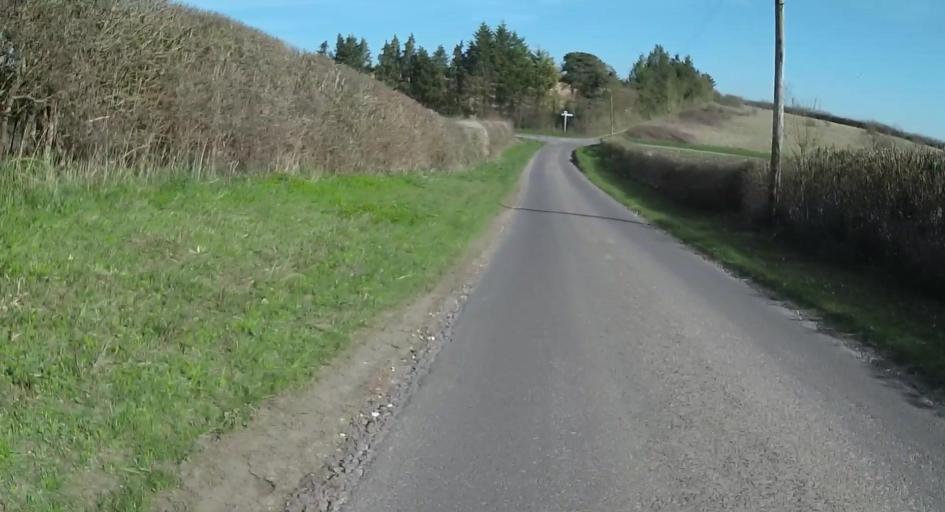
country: GB
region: England
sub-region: Hampshire
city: Highclere
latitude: 51.2598
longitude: -1.3842
